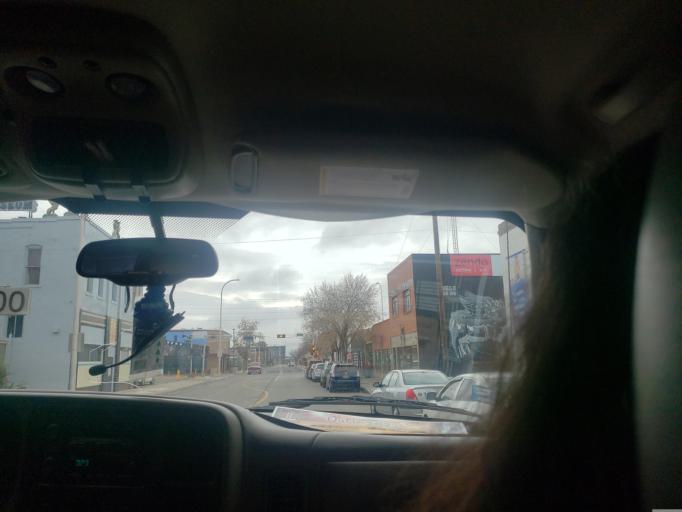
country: US
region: New Mexico
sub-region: Bernalillo County
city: Albuquerque
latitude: 35.0810
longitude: -106.6499
